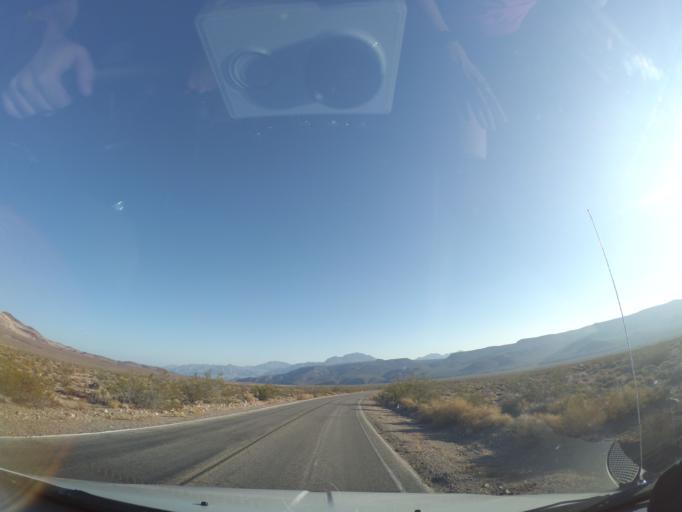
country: US
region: Nevada
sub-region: Nye County
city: Beatty
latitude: 36.2456
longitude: -116.6828
